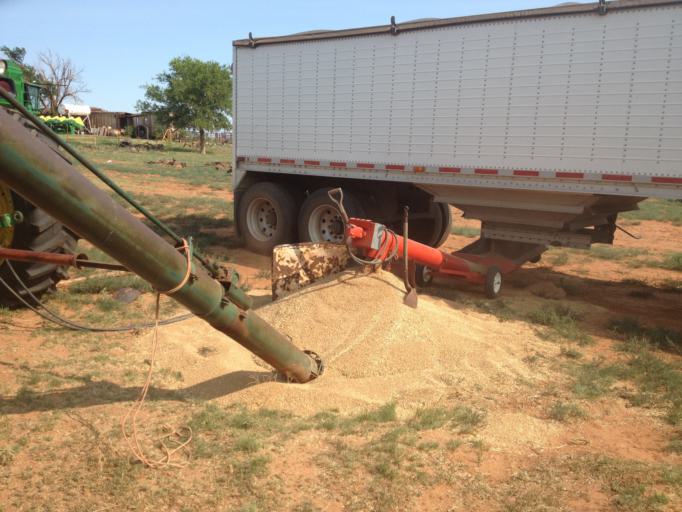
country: US
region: Texas
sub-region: Childress County
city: Childress
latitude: 34.3913
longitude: -100.4042
